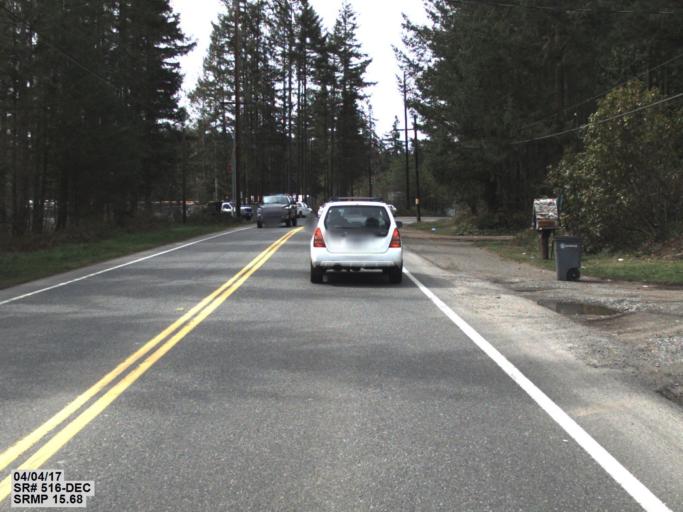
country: US
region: Washington
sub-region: King County
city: Maple Valley
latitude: 47.3584
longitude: -122.0313
